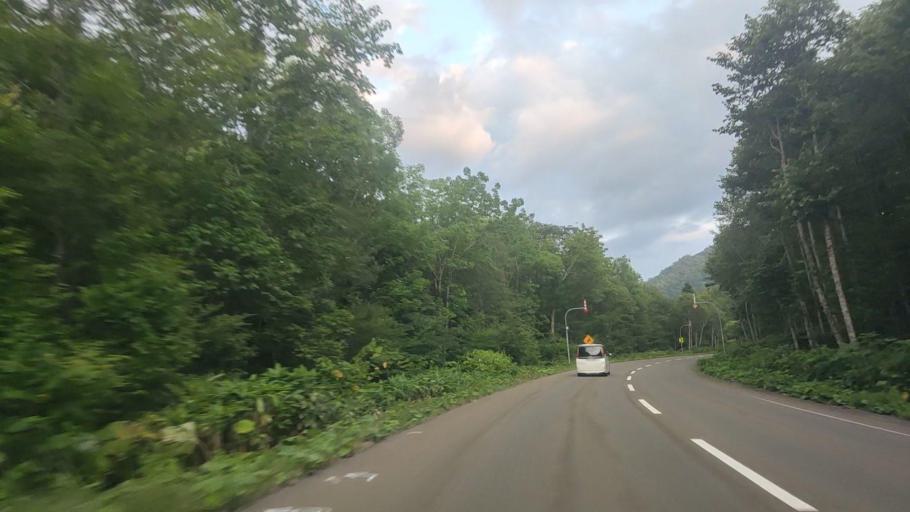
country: JP
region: Hokkaido
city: Ashibetsu
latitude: 43.3748
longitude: 142.2229
